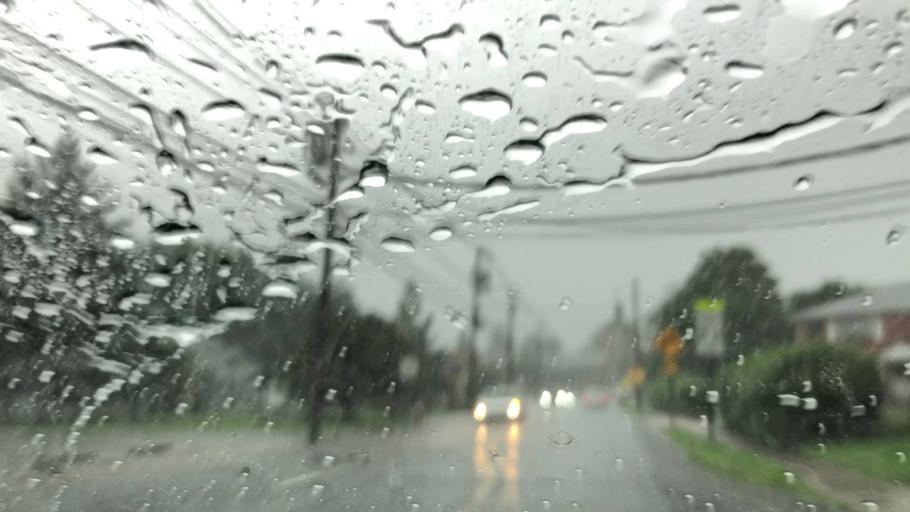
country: US
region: New Jersey
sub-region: Bergen County
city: Rochelle Park
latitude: 40.9036
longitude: -74.0781
